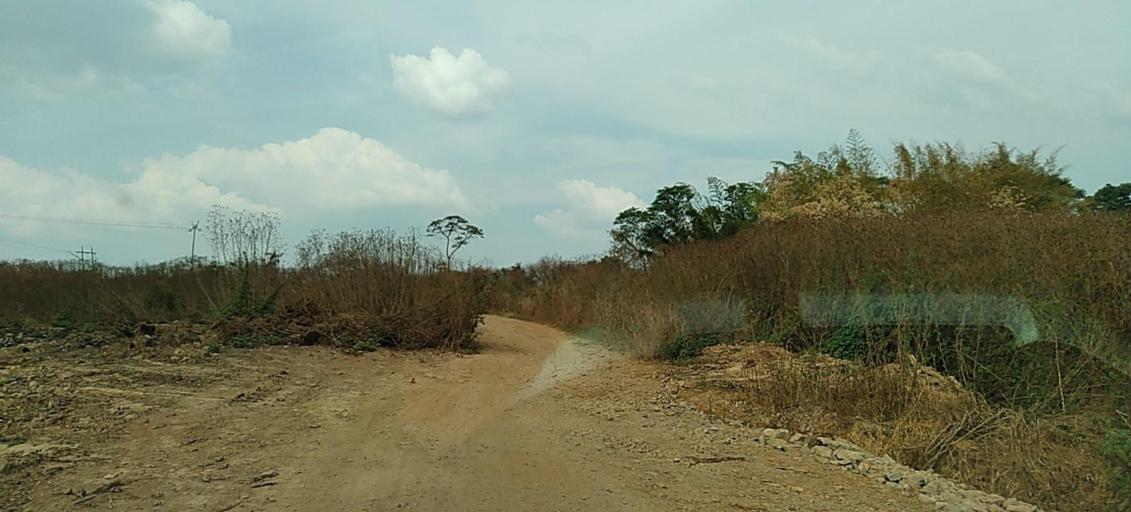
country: ZM
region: Copperbelt
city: Chililabombwe
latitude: -12.3977
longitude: 27.8036
